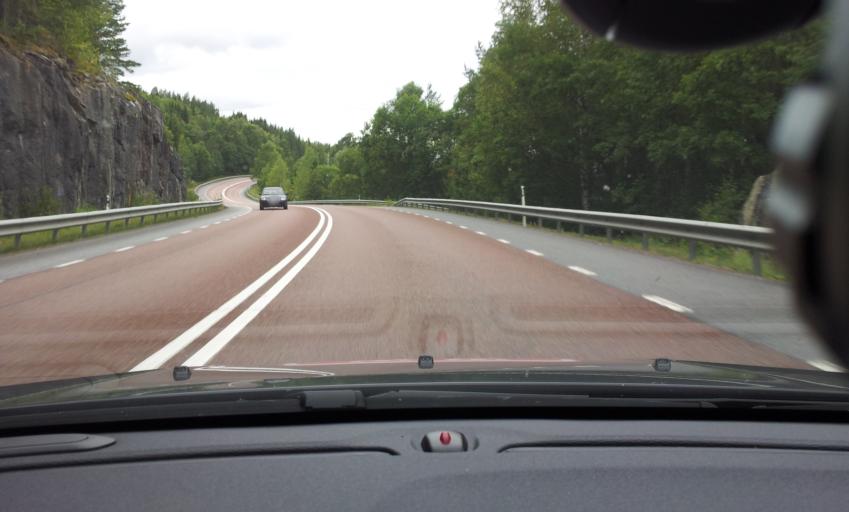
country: SE
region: Jaemtland
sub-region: Braecke Kommun
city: Braecke
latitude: 62.9535
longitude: 15.1562
